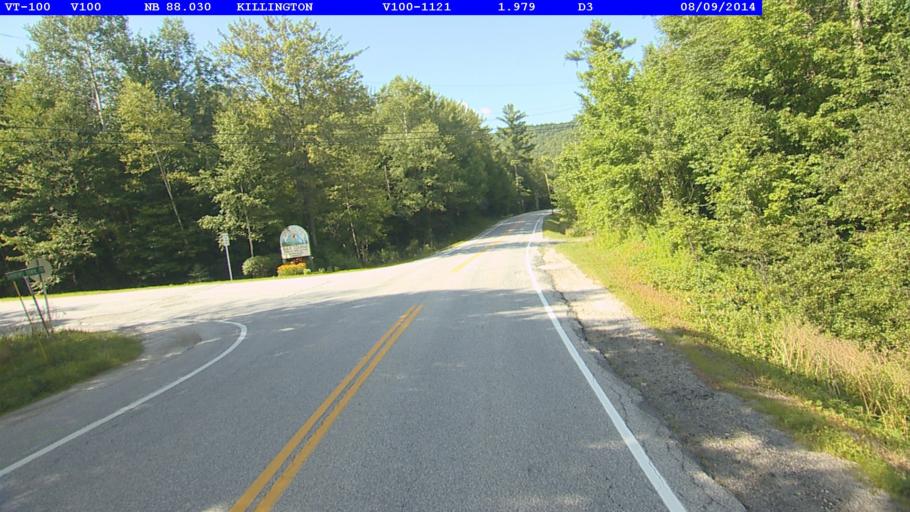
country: US
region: Vermont
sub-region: Rutland County
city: Rutland
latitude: 43.6937
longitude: -72.8142
